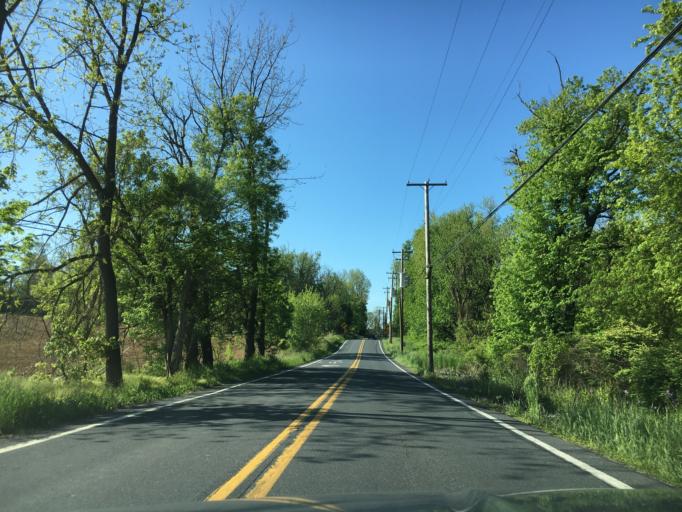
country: US
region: Pennsylvania
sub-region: Lehigh County
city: Catasauqua
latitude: 40.6713
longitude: -75.4306
